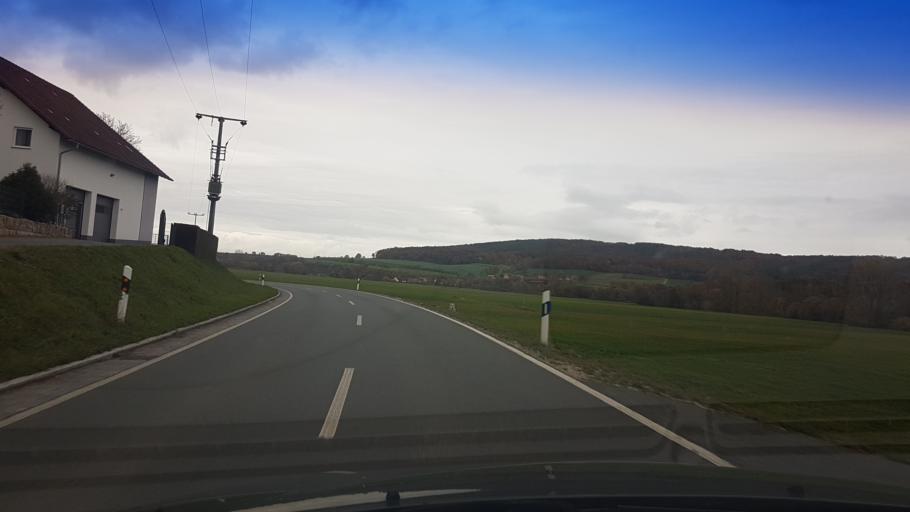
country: DE
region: Bavaria
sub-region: Upper Franconia
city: Rattelsdorf
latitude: 50.0506
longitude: 10.8731
